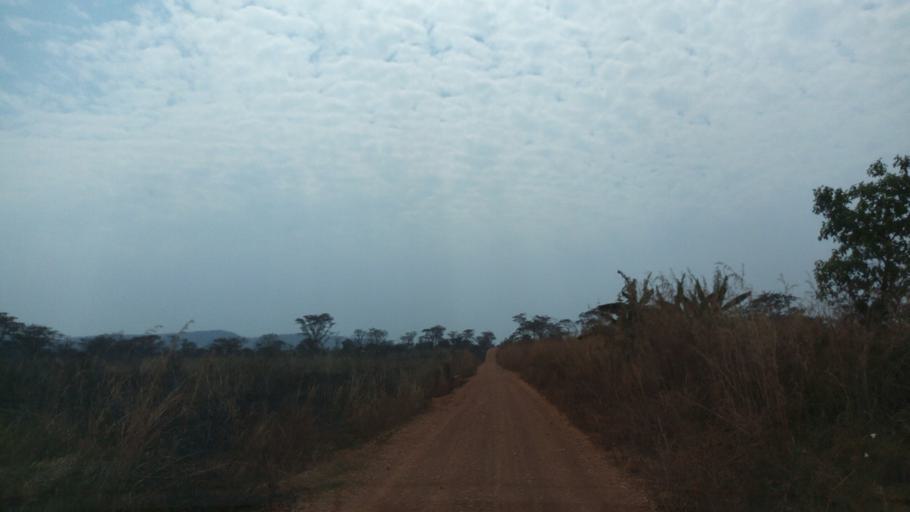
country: ZM
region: Northern
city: Kaputa
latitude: -8.2916
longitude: 29.0107
